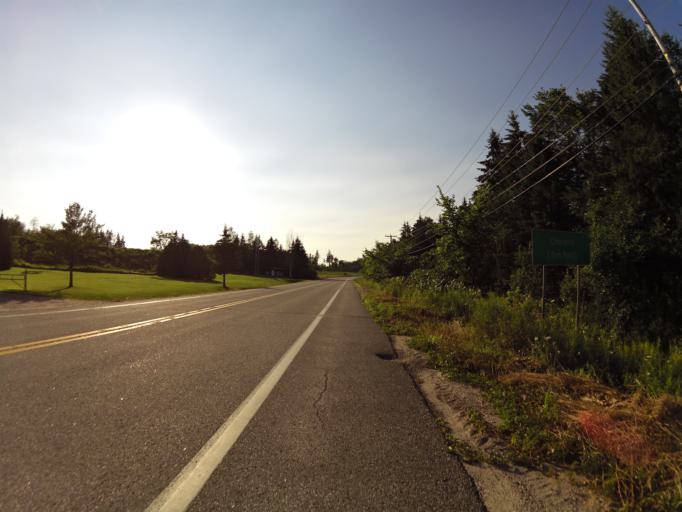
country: CA
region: Quebec
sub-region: Outaouais
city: Wakefield
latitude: 45.5821
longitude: -75.8847
